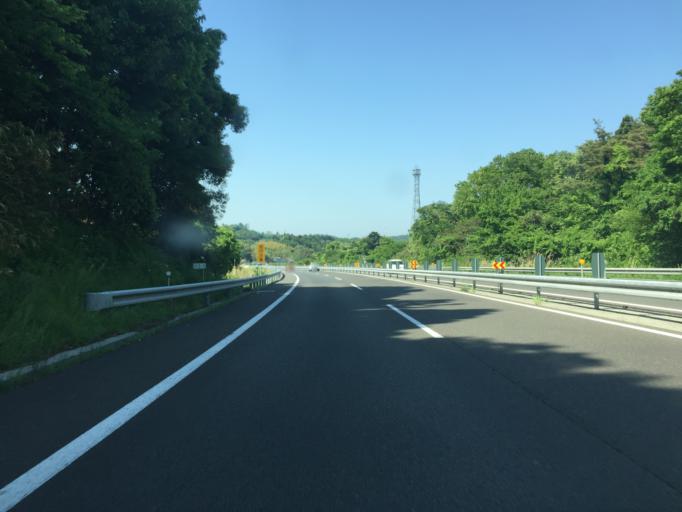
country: JP
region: Miyagi
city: Matsushima
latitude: 38.3800
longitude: 141.0343
